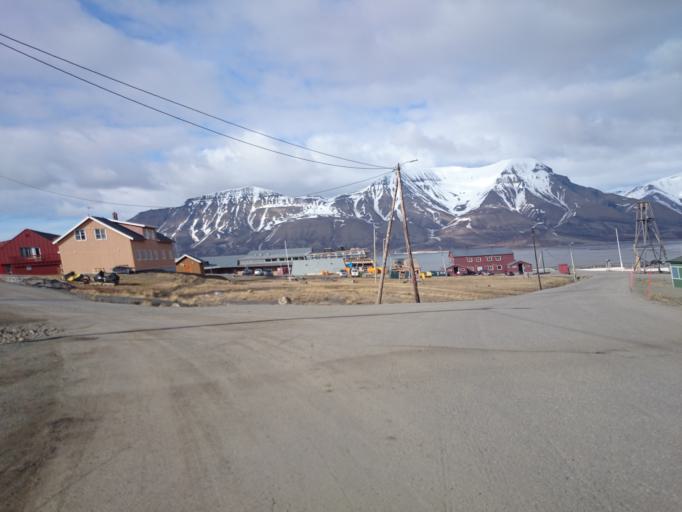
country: SJ
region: Svalbard
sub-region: Spitsbergen
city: Longyearbyen
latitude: 78.2211
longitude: 15.6227
